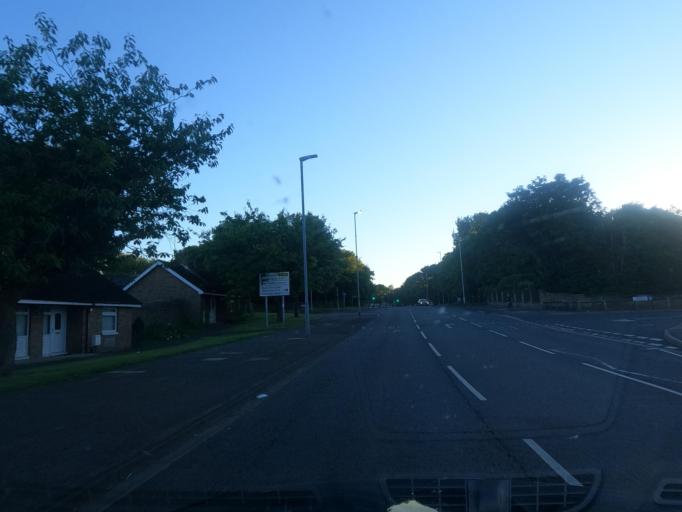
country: GB
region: England
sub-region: Northumberland
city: Blyth
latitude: 55.1299
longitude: -1.5472
